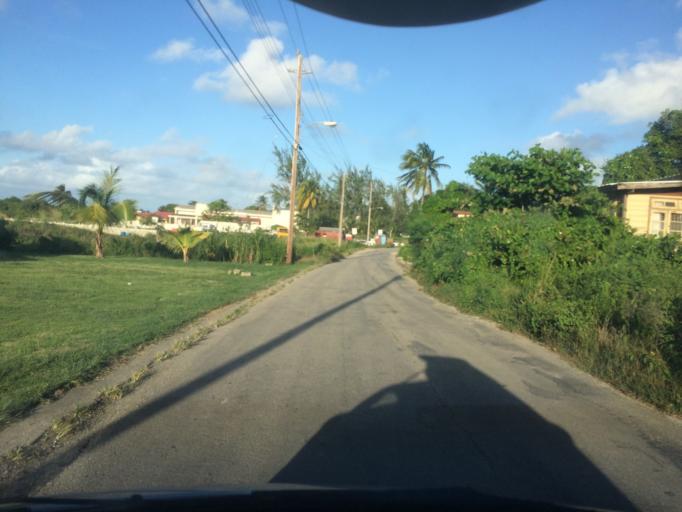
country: BB
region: Saint Lucy
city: Checker Hall
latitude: 13.3131
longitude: -59.6364
